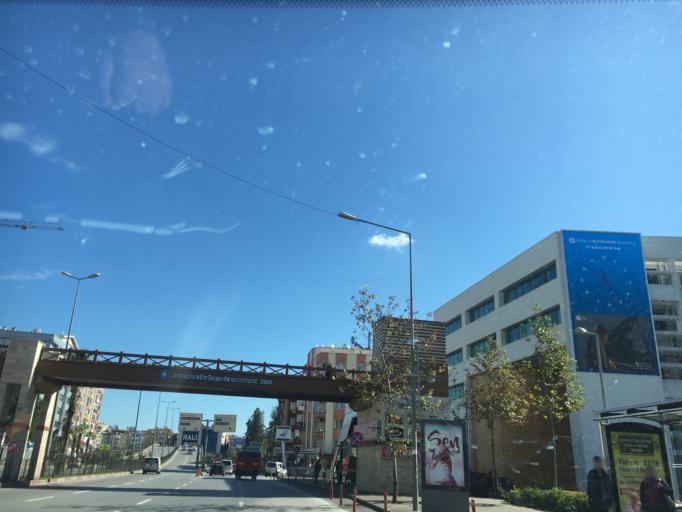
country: TR
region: Antalya
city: Antalya
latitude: 36.8958
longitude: 30.7098
